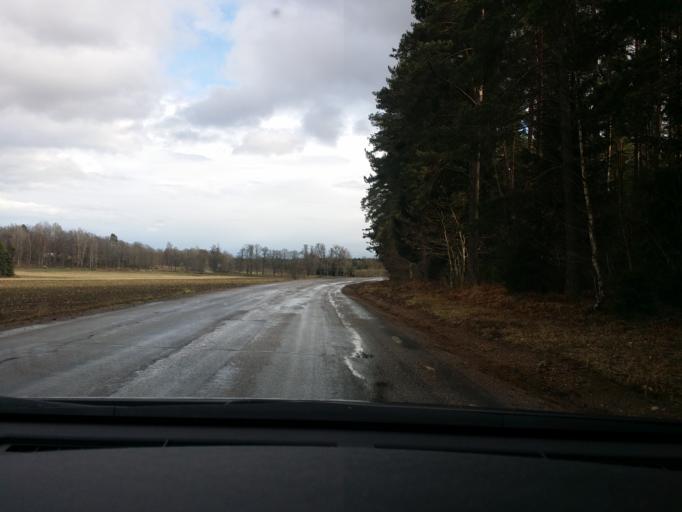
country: SE
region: Soedermanland
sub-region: Eskilstuna Kommun
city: Arla
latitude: 59.3108
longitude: 16.6814
